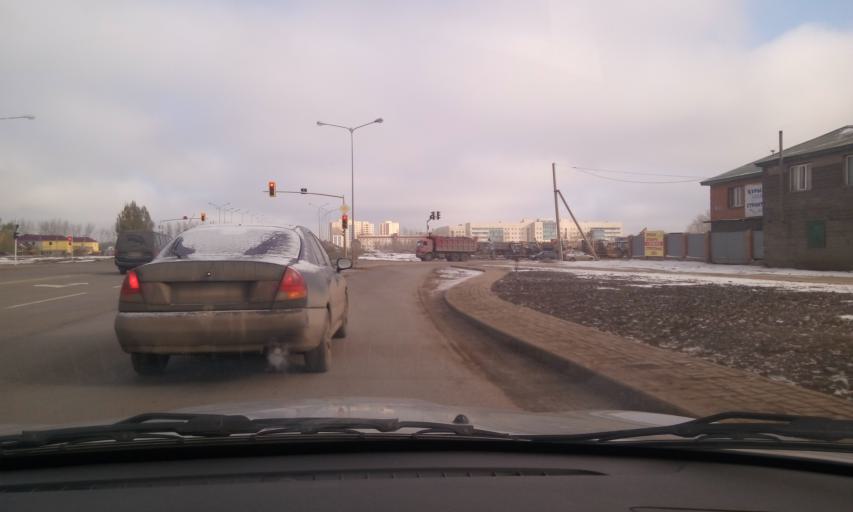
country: KZ
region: Astana Qalasy
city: Astana
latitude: 51.1364
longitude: 71.5211
